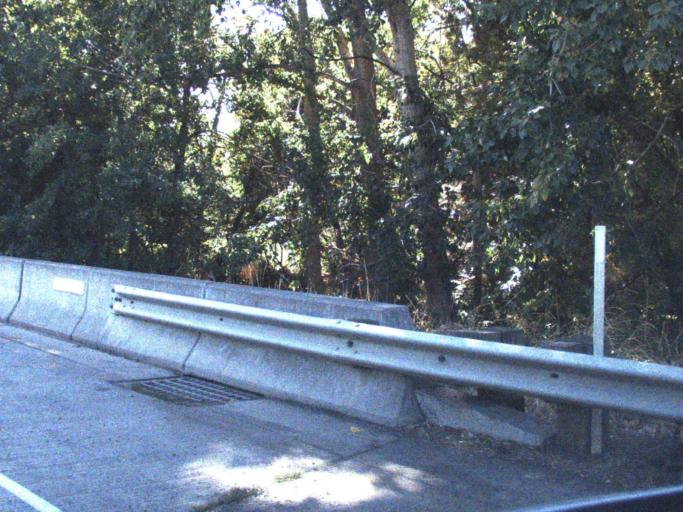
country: US
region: Washington
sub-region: Walla Walla County
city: College Place
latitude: 46.0224
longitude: -118.3891
